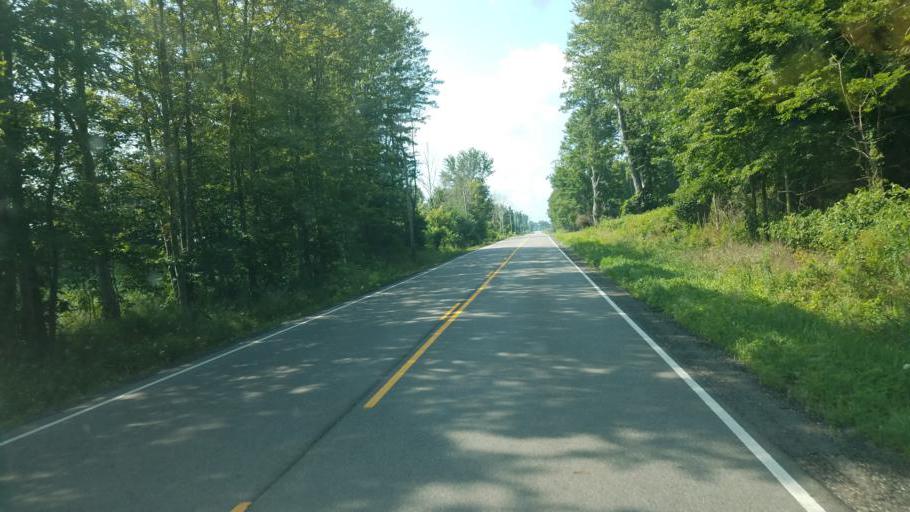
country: US
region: Ohio
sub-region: Licking County
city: Utica
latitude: 40.2774
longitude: -82.5153
